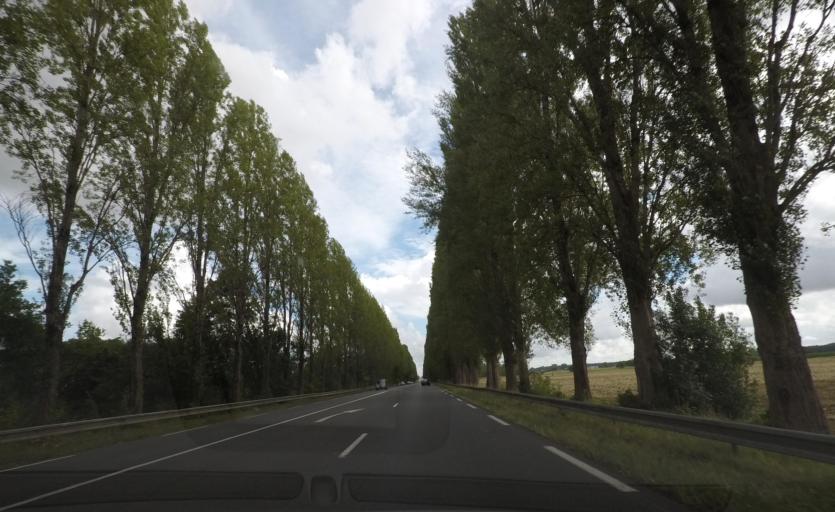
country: FR
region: Pays de la Loire
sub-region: Departement de Maine-et-Loire
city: Corze
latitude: 47.5386
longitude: -0.4062
